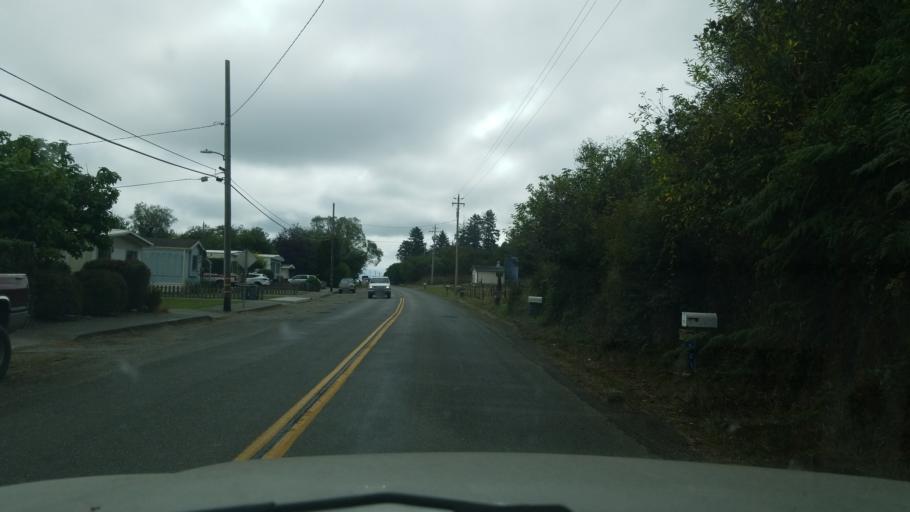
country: US
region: California
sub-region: Humboldt County
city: Ferndale
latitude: 40.5813
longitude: -124.2829
